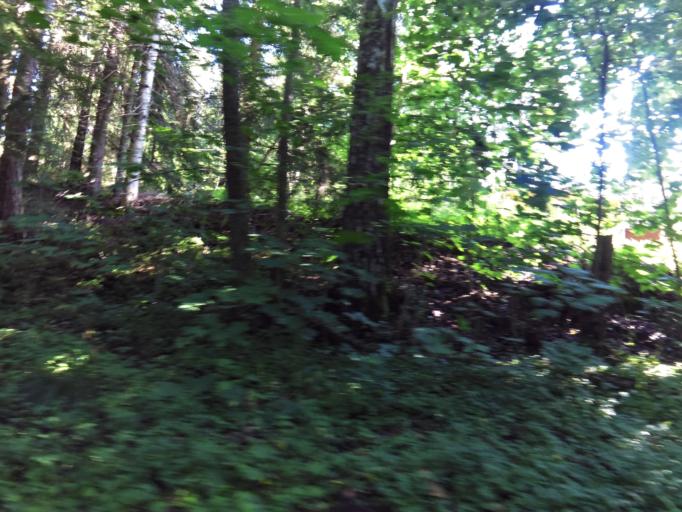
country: FI
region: Uusimaa
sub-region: Helsinki
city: Espoo
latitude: 60.1528
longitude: 24.6878
